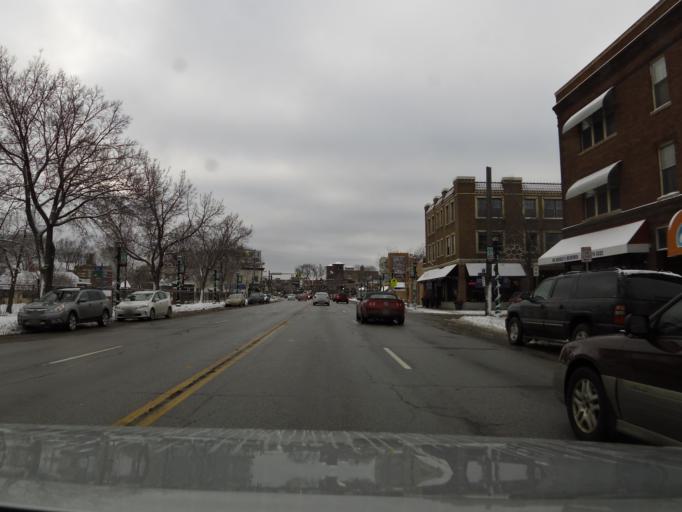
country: US
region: Minnesota
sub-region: Hennepin County
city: Minneapolis
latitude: 44.9566
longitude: -93.2961
